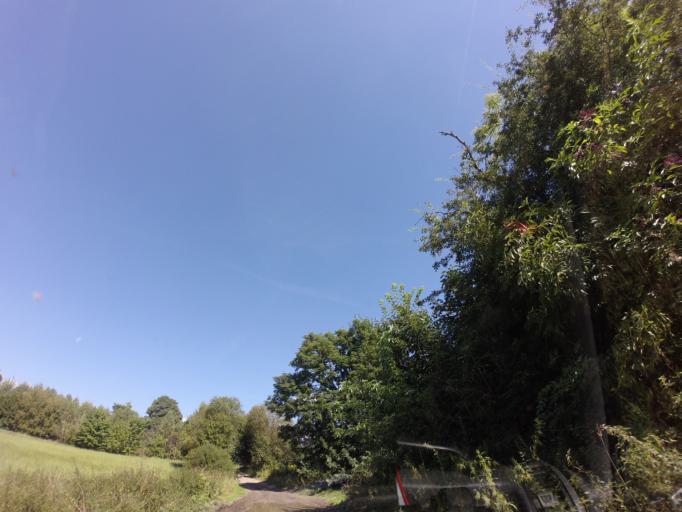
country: PL
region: West Pomeranian Voivodeship
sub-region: Powiat choszczenski
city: Recz
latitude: 53.1676
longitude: 15.5772
